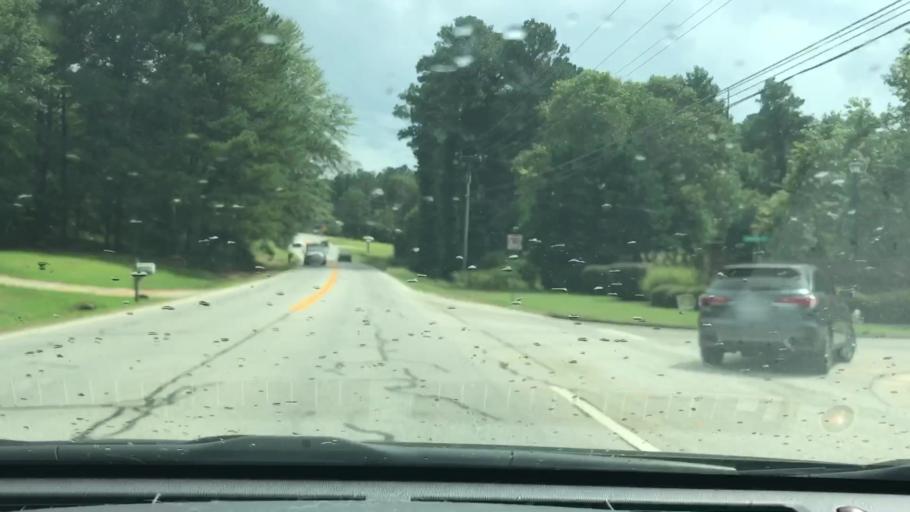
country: US
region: Georgia
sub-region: Walton County
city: Walnut Grove
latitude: 33.7496
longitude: -83.8532
